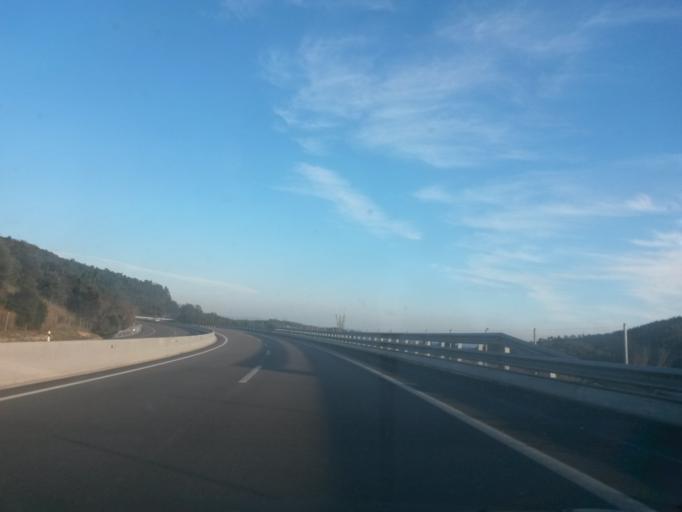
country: ES
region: Catalonia
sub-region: Provincia de Girona
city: Santa Coloma de Farners
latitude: 41.8733
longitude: 2.6173
